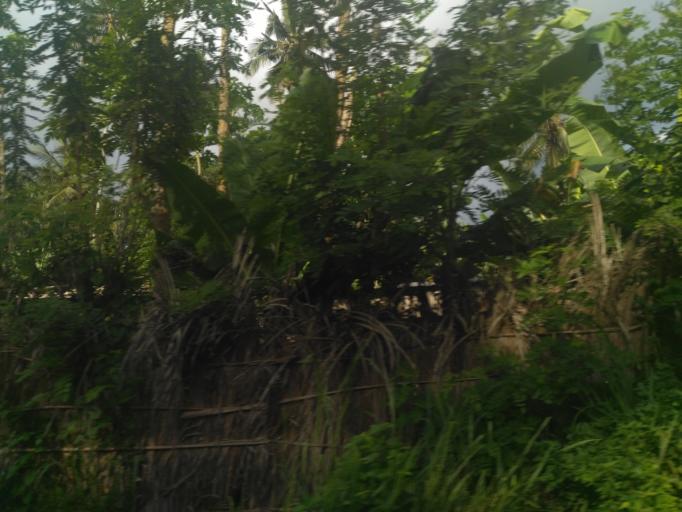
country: TZ
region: Zanzibar Central/South
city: Koani
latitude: -6.1082
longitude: 39.3017
